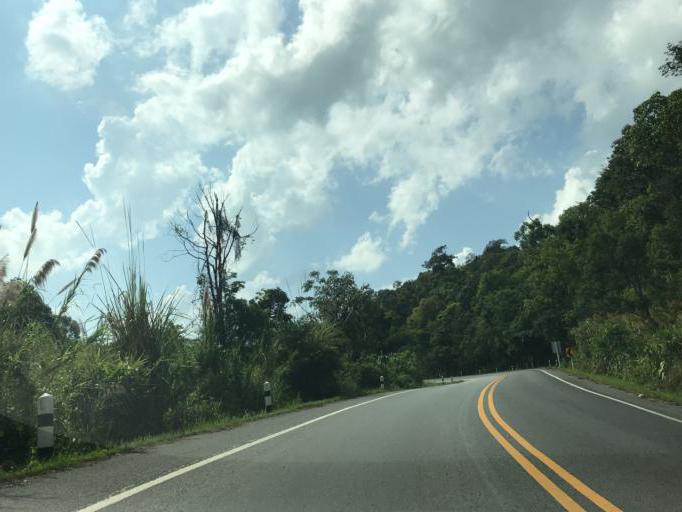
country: TH
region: Phayao
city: Phayao
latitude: 19.0620
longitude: 99.7745
